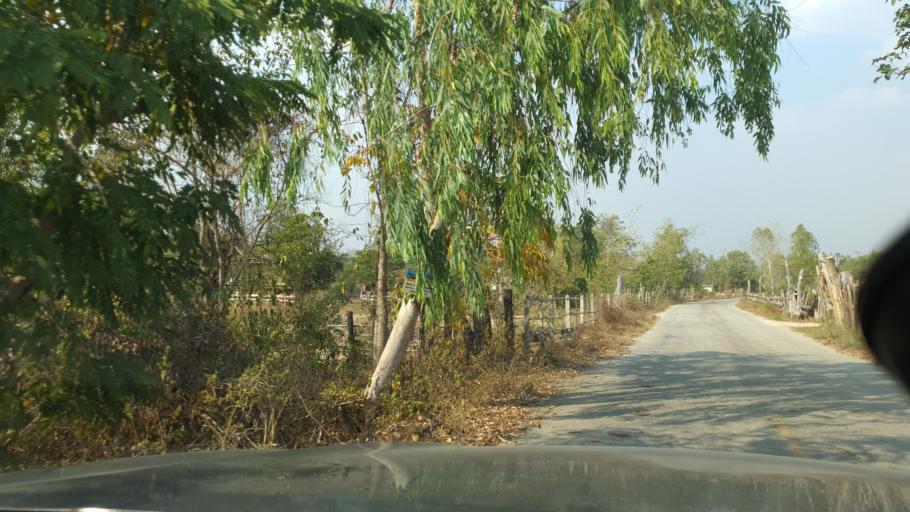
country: TH
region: Sukhothai
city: Ban Dan Lan Hoi
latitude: 17.0122
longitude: 99.5582
